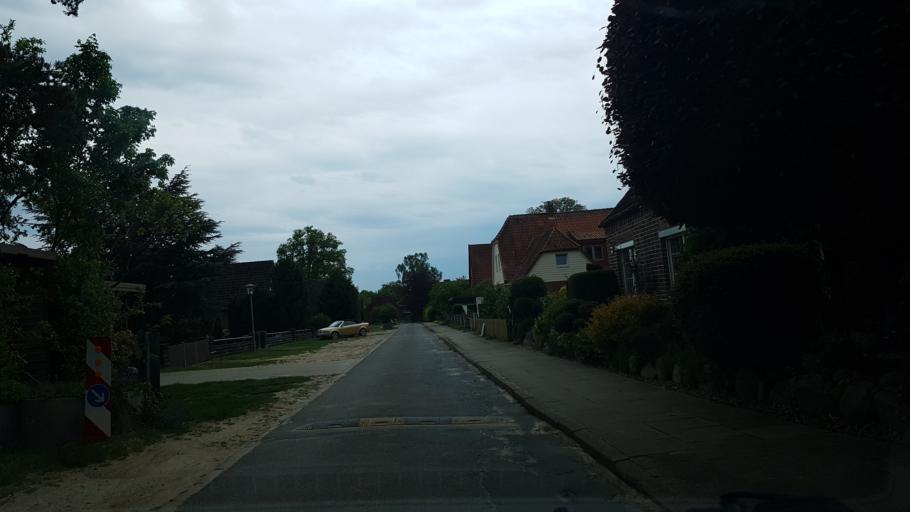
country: DE
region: Lower Saxony
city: Vastorf
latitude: 53.2096
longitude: 10.5422
